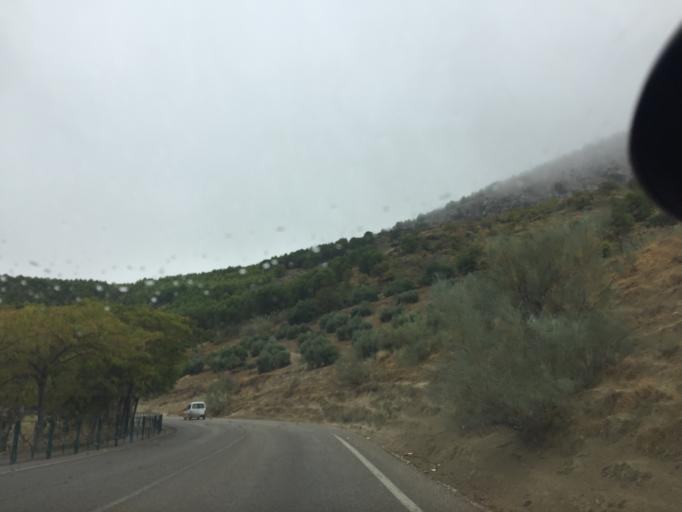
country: ES
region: Andalusia
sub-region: Provincia de Jaen
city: Jimena
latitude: 37.8403
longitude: -3.4794
